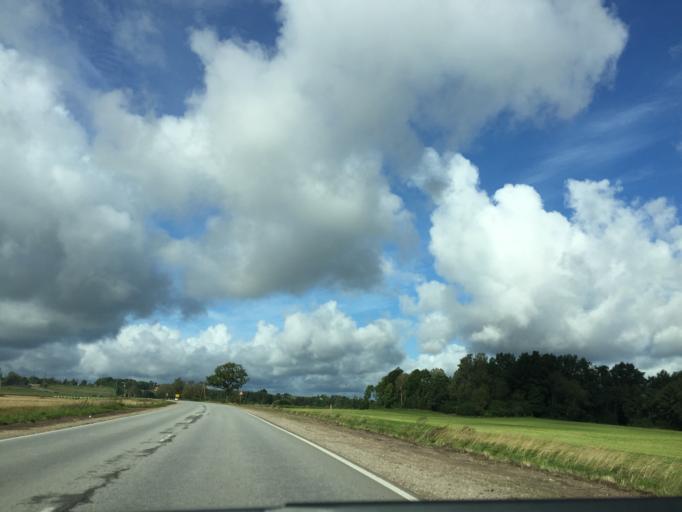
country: LV
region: Engure
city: Smarde
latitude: 56.9214
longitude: 23.2911
